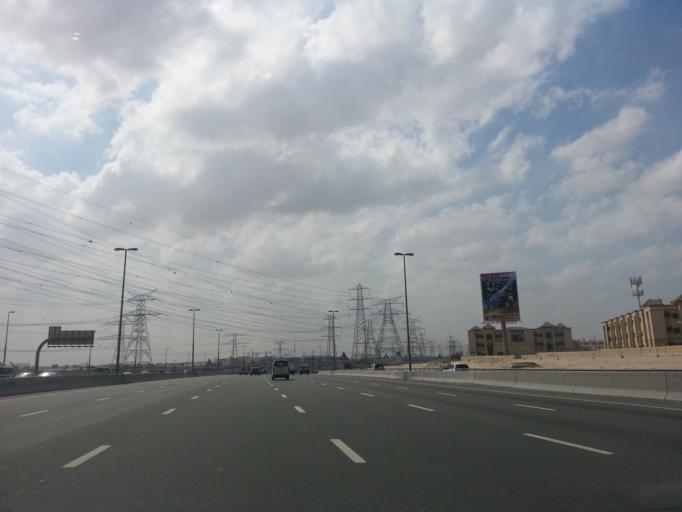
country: AE
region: Dubai
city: Dubai
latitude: 25.1389
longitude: 55.2602
